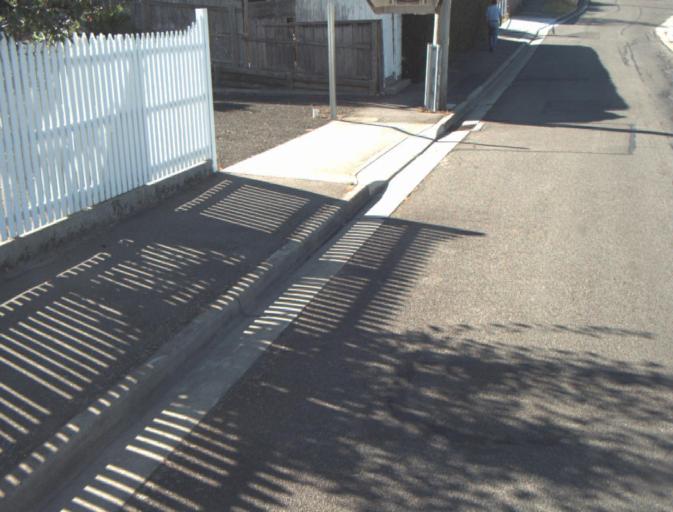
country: AU
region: Tasmania
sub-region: Launceston
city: Newnham
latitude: -41.4059
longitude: 147.1252
